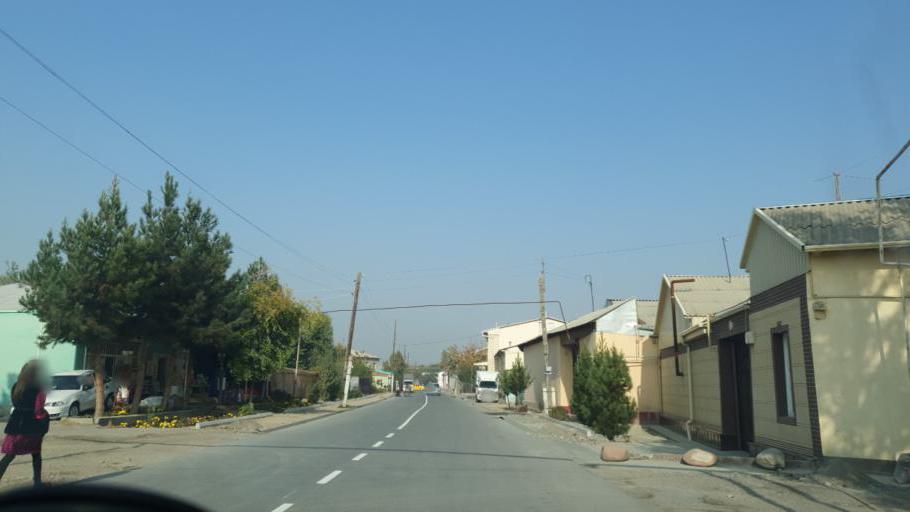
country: UZ
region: Fergana
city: Qo`qon
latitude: 40.5822
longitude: 70.9108
